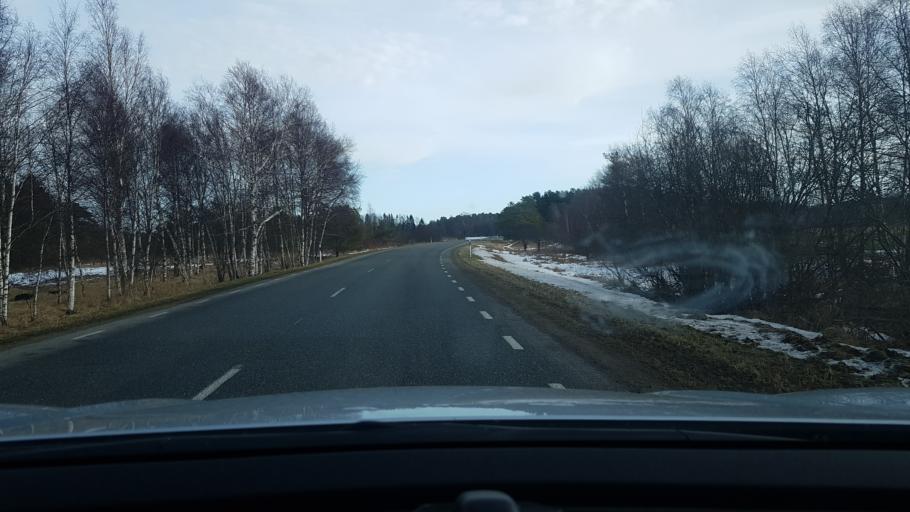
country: EE
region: Saare
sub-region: Kuressaare linn
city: Kuressaare
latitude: 58.4279
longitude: 22.6820
